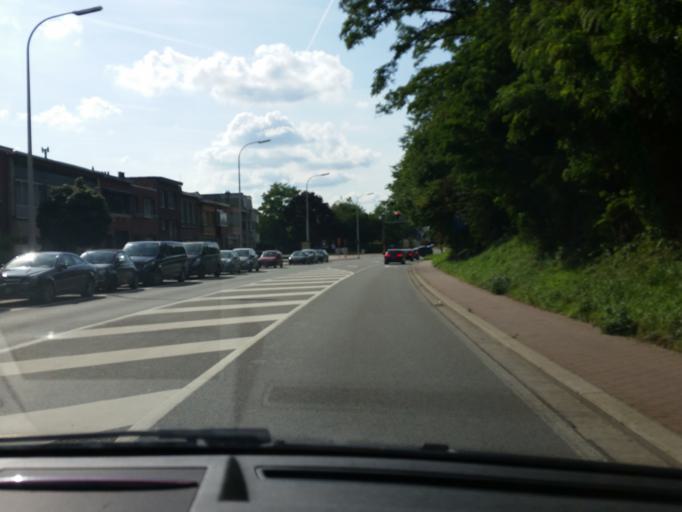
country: BE
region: Flanders
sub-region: Provincie Antwerpen
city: Mortsel
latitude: 51.1739
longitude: 4.4516
